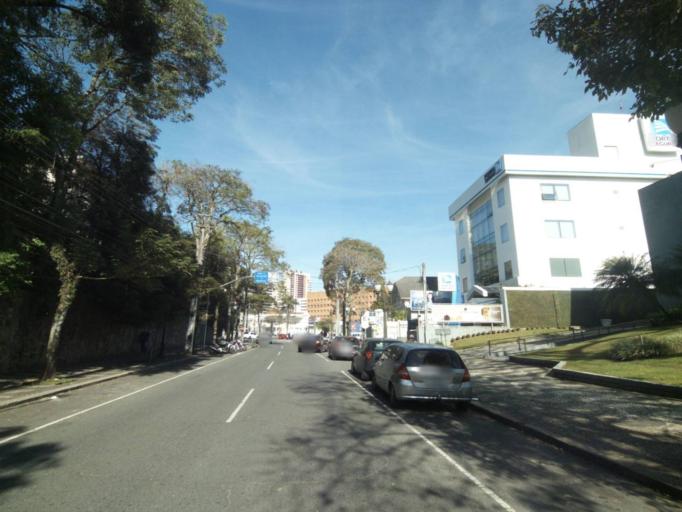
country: BR
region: Parana
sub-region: Curitiba
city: Curitiba
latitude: -25.4401
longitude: -49.2831
